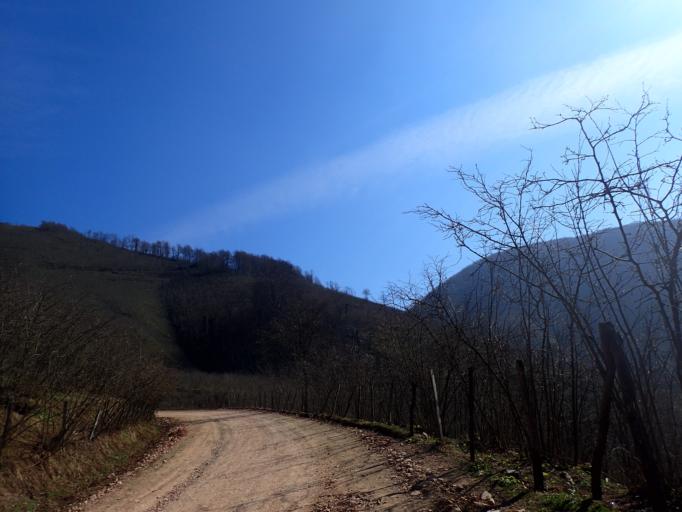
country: TR
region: Ordu
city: Catalpinar
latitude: 40.8639
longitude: 37.4962
